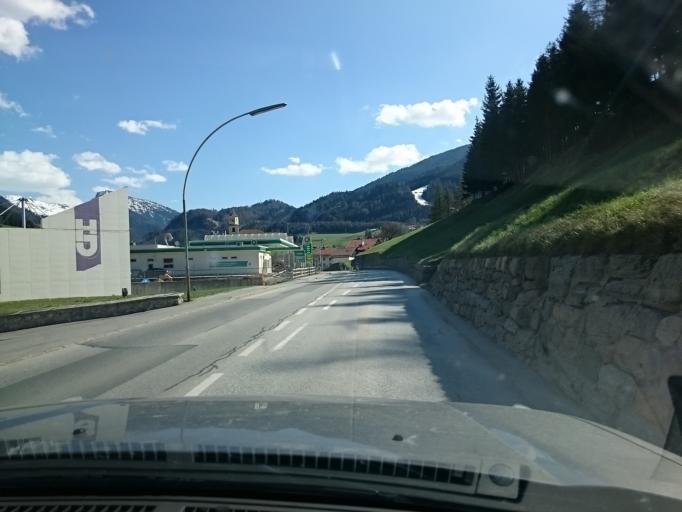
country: AT
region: Tyrol
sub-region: Politischer Bezirk Innsbruck Land
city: Steinach am Brenner
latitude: 47.0961
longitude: 11.4651
